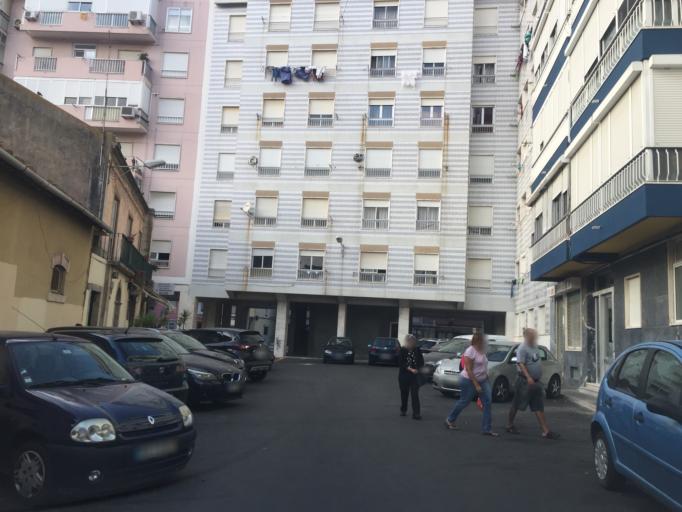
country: PT
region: Lisbon
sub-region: Odivelas
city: Pontinha
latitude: 38.7502
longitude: -9.1987
